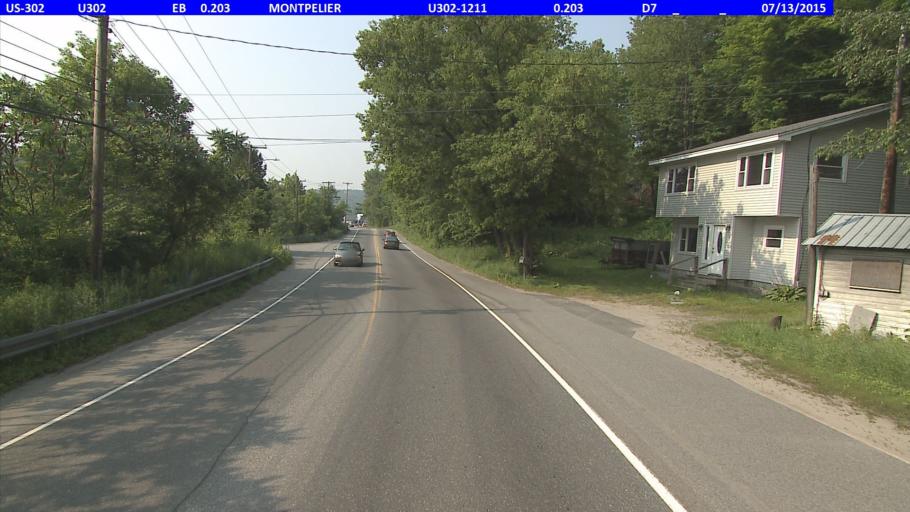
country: US
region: Vermont
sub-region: Washington County
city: Montpelier
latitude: 44.2440
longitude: -72.5515
